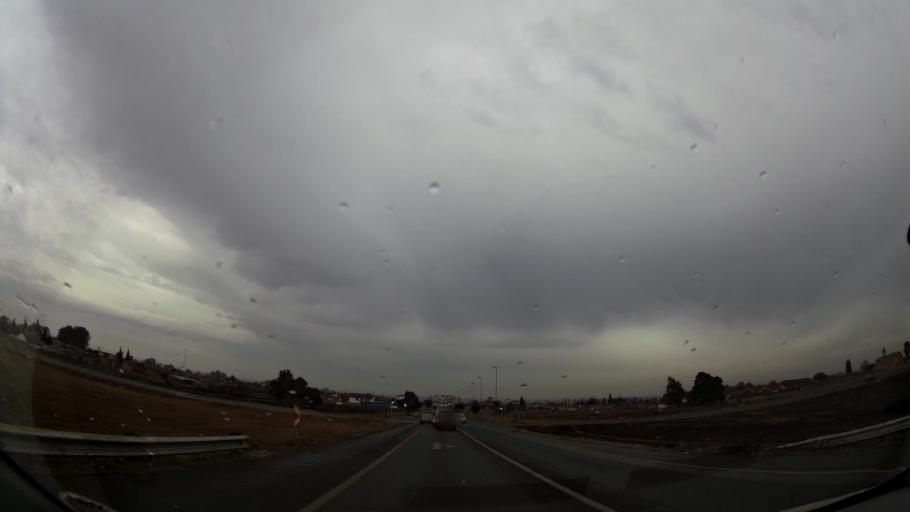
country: ZA
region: Gauteng
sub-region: Ekurhuleni Metropolitan Municipality
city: Germiston
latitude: -26.3216
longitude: 28.1897
